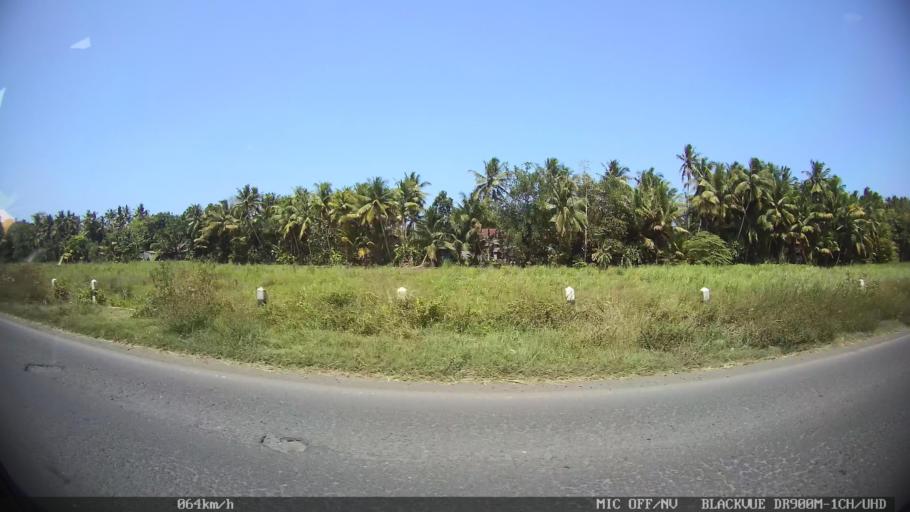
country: ID
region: Daerah Istimewa Yogyakarta
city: Srandakan
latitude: -7.9432
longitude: 110.1685
